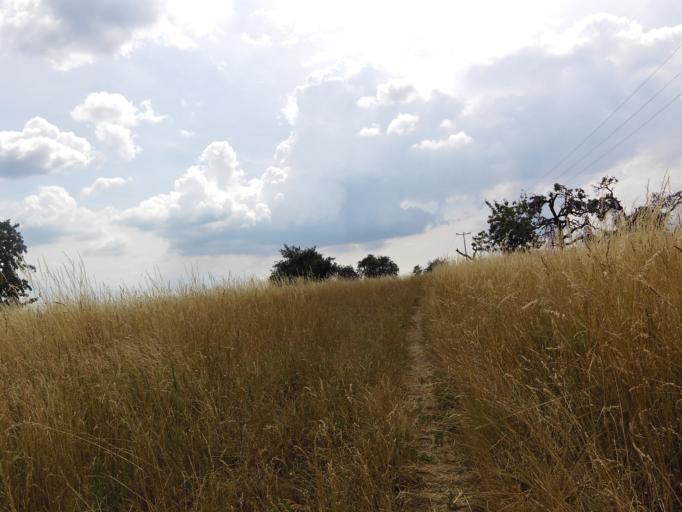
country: DE
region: Bavaria
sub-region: Regierungsbezirk Unterfranken
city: Gerbrunn
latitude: 49.7741
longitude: 9.9871
